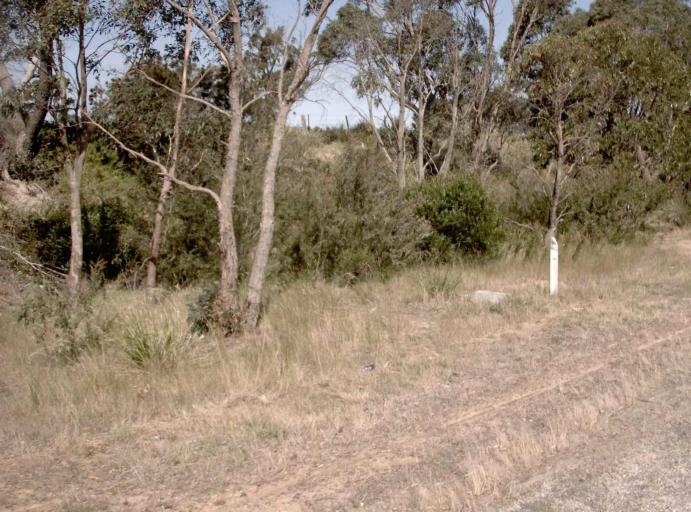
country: AU
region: Victoria
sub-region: Wellington
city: Sale
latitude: -38.3411
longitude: 147.1668
